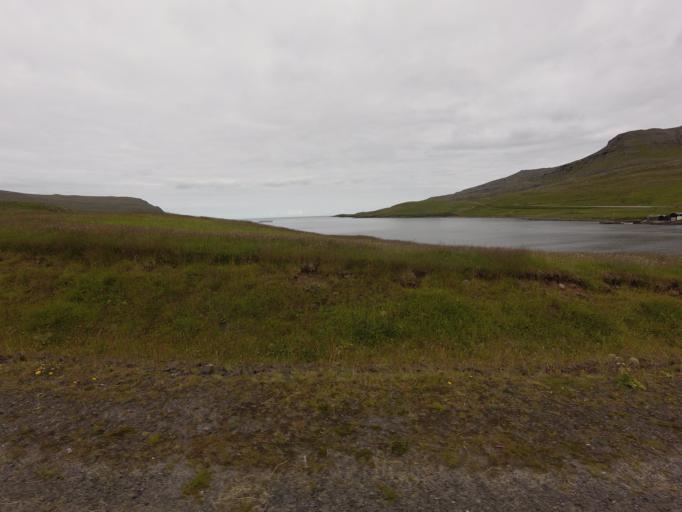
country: FO
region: Suduroy
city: Tvoroyri
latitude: 61.5357
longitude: -6.8119
